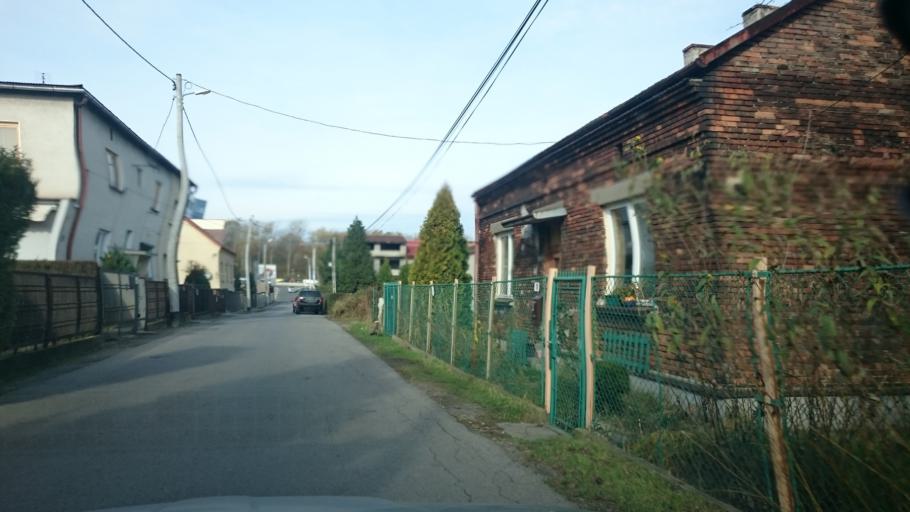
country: PL
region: Lesser Poland Voivodeship
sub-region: Krakow
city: Krakow
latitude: 50.0259
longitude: 19.9647
